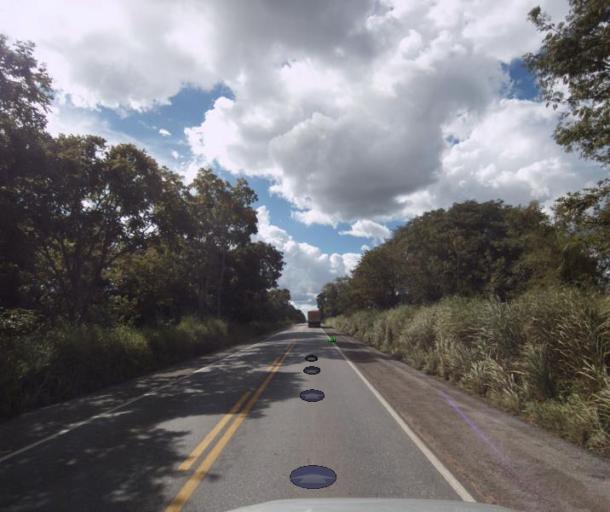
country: BR
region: Goias
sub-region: Porangatu
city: Porangatu
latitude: -13.2759
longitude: -49.1298
